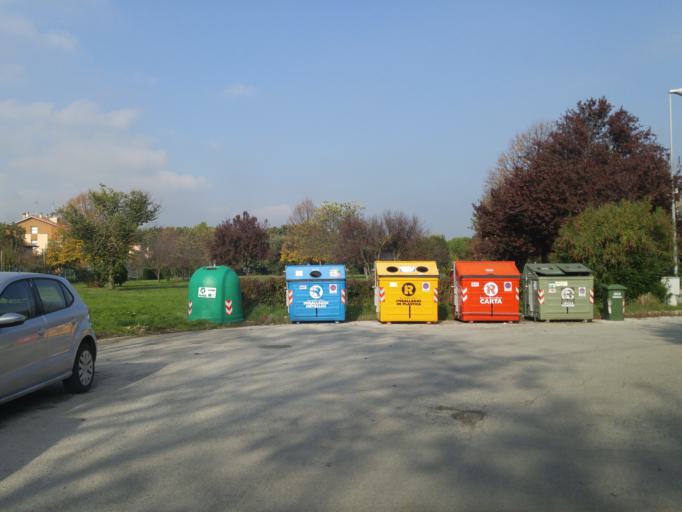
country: IT
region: The Marches
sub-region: Provincia di Pesaro e Urbino
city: Fano
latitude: 43.8282
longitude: 13.0095
